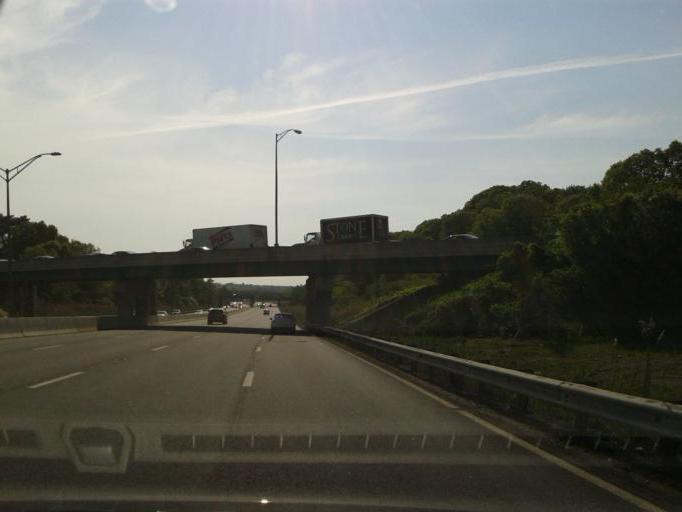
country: US
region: Massachusetts
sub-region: Middlesex County
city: Weston
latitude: 42.3390
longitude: -71.2735
